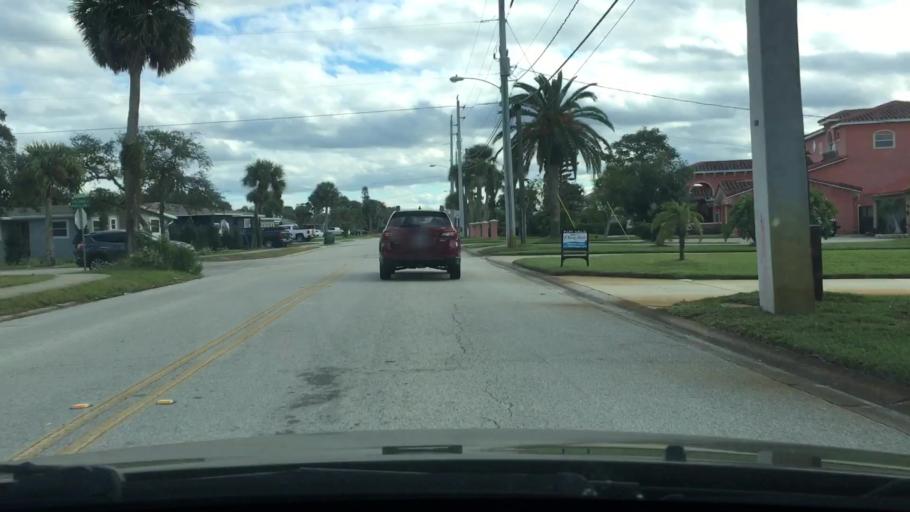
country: US
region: Florida
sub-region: Volusia County
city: Ormond Beach
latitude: 29.2715
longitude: -81.0388
